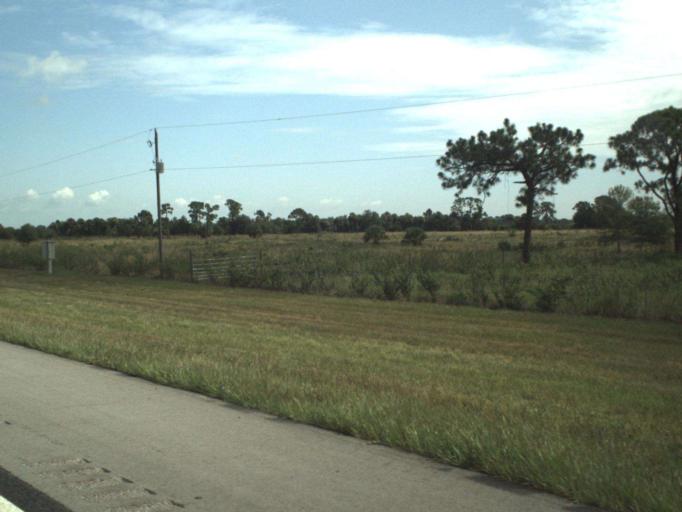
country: US
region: Florida
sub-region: Saint Lucie County
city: Lakewood Park
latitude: 27.4951
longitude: -80.4392
